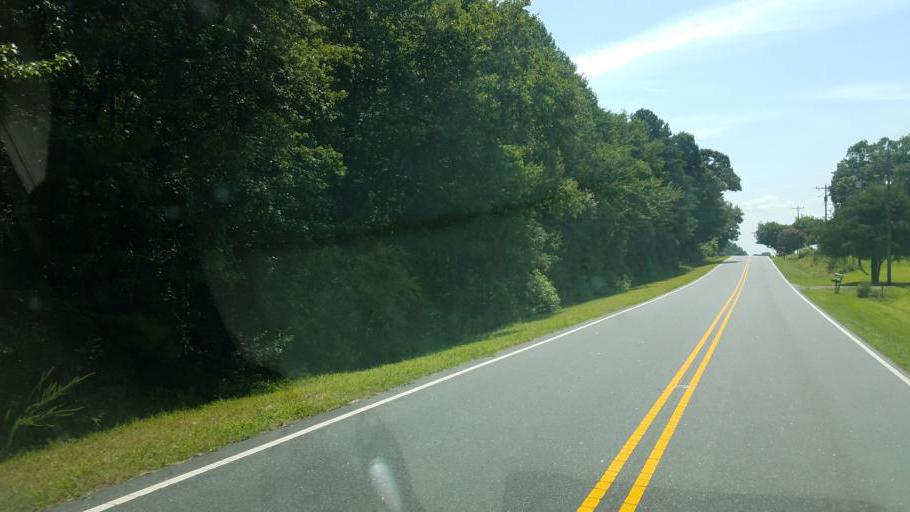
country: US
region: North Carolina
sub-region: Gaston County
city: Cherryville
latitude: 35.5128
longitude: -81.4656
